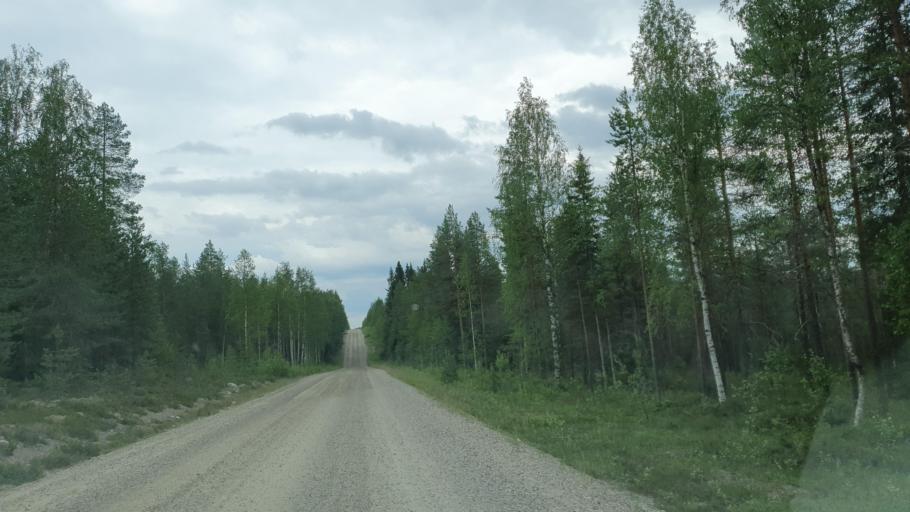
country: FI
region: Kainuu
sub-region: Kehys-Kainuu
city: Kuhmo
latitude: 64.7534
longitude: 29.8643
